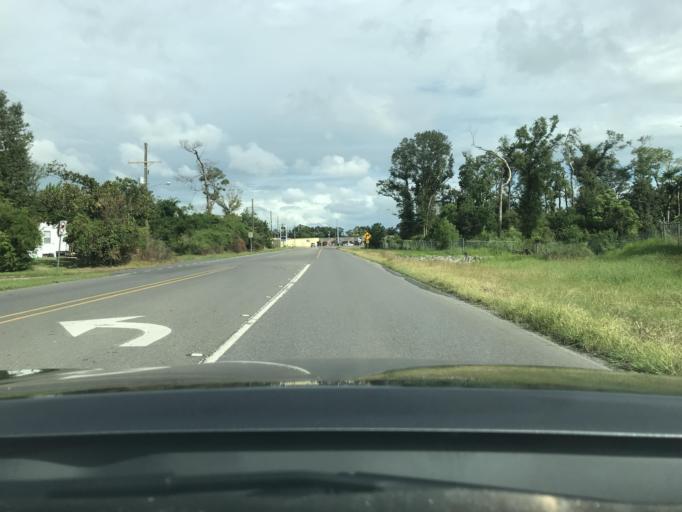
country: US
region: Louisiana
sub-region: Calcasieu Parish
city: Westlake
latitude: 30.2496
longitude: -93.2690
